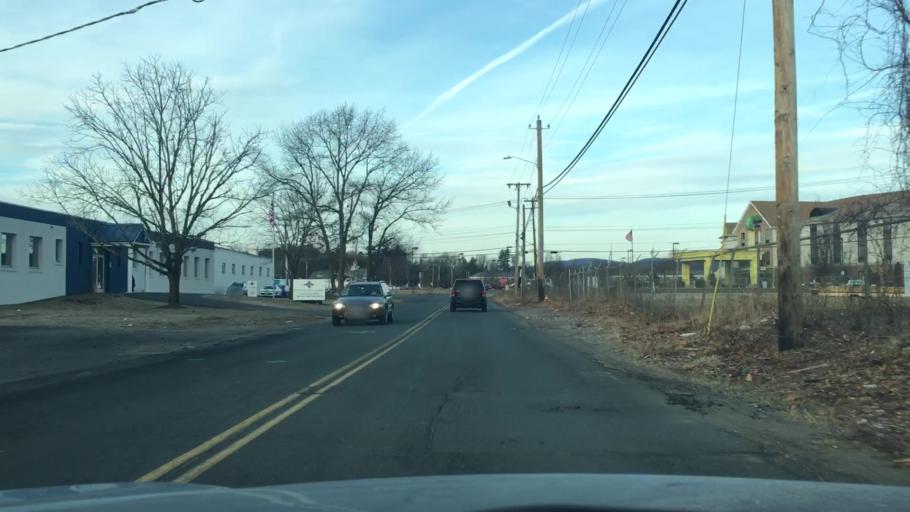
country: US
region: Massachusetts
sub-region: Hampden County
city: Westfield
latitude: 42.1416
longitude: -72.7288
